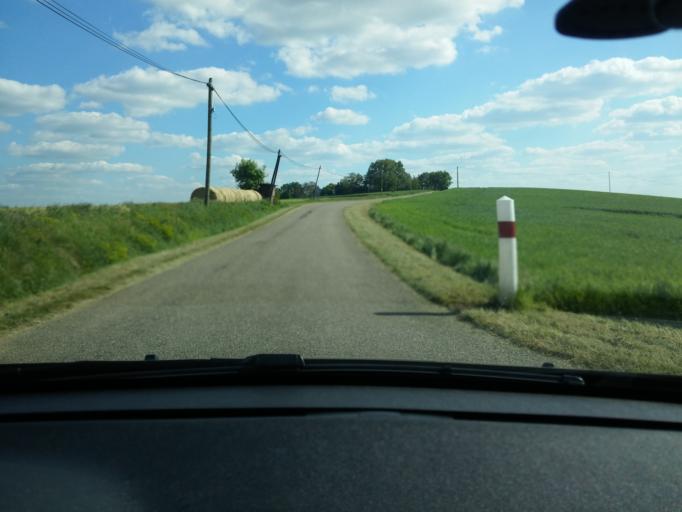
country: FR
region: Aquitaine
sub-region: Departement du Lot-et-Garonne
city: Laplume
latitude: 44.0915
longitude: 0.4705
